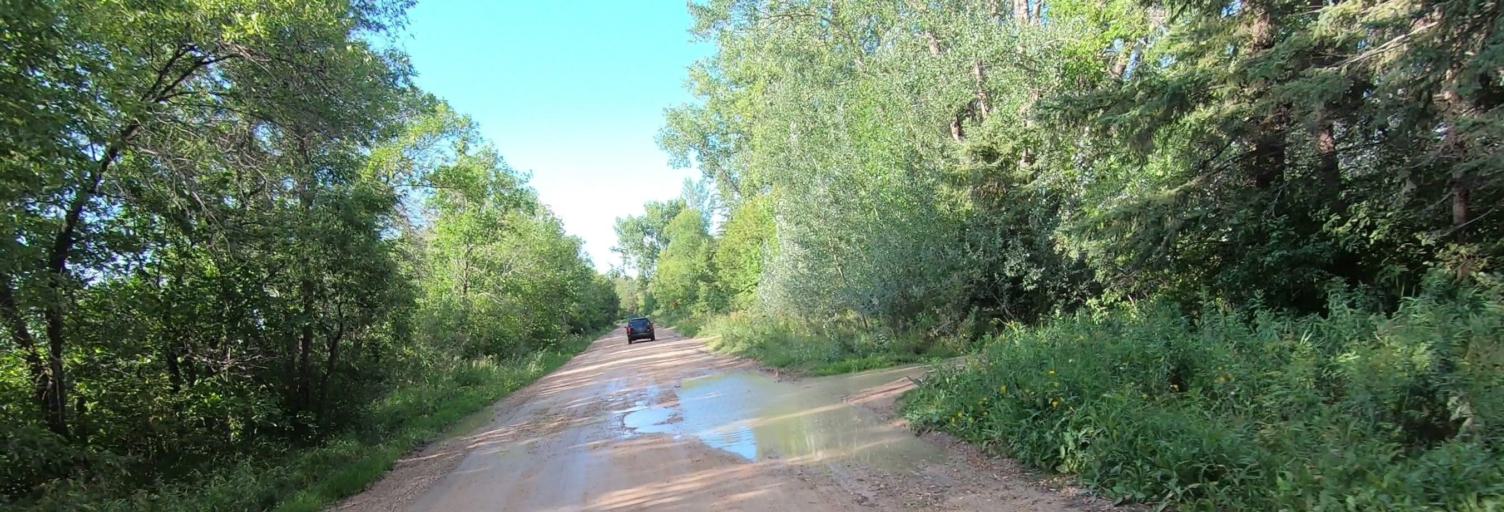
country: CA
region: Manitoba
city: Selkirk
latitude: 50.2671
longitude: -96.8494
